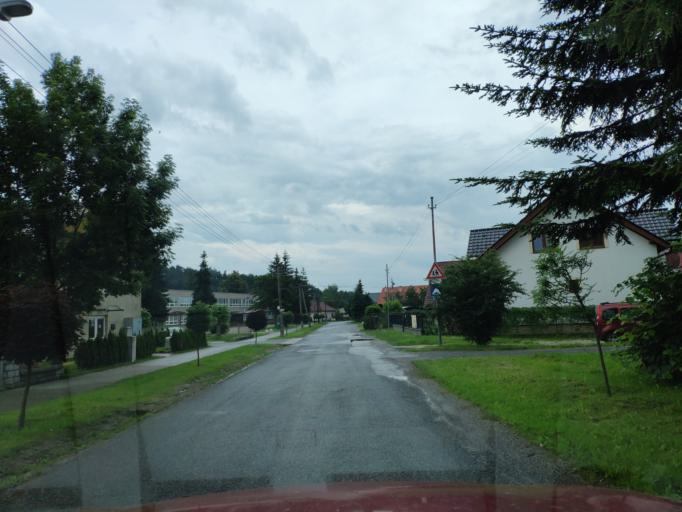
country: SK
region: Presovsky
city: Sabinov
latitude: 49.0022
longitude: 21.0808
